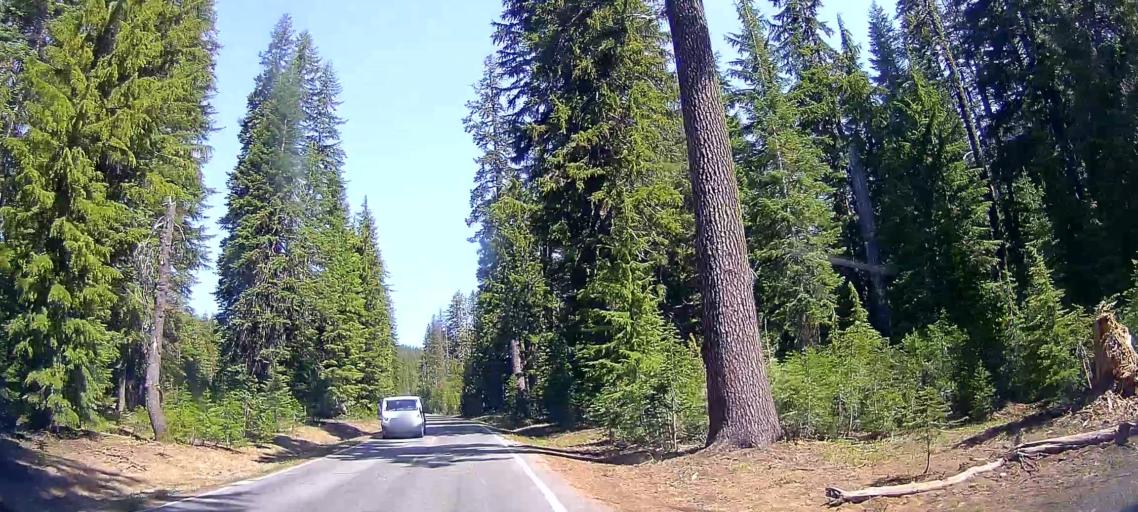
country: US
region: Oregon
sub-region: Jackson County
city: Shady Cove
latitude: 42.8914
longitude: -122.1326
